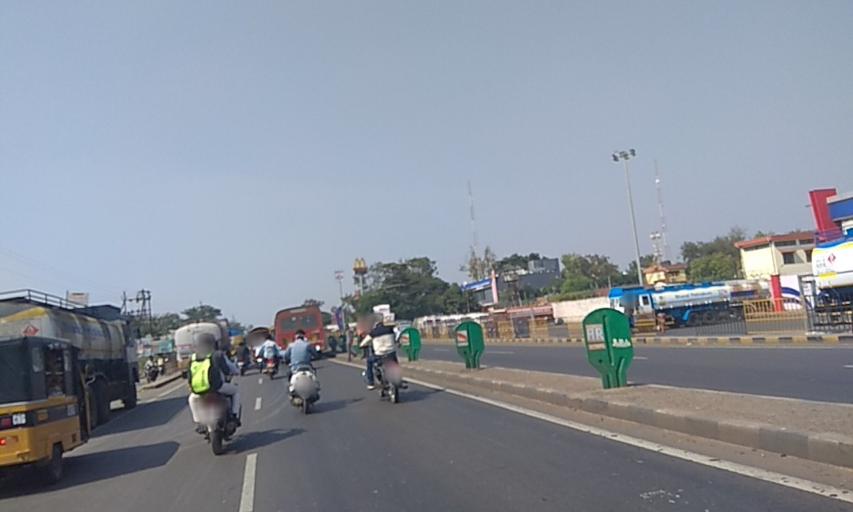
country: IN
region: Maharashtra
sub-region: Pune Division
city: Lohogaon
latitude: 18.4901
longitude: 74.0150
